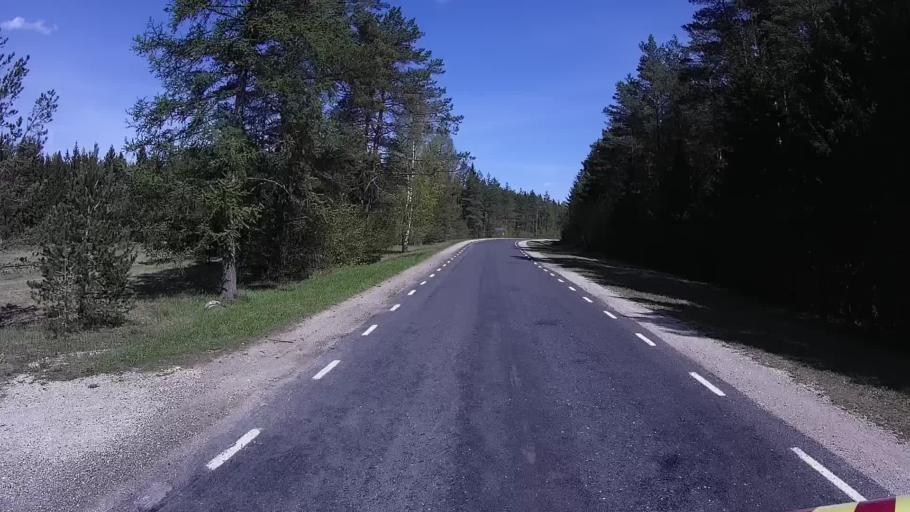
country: EE
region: Laeaene
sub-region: Ridala Parish
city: Uuemoisa
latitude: 59.0330
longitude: 23.8214
